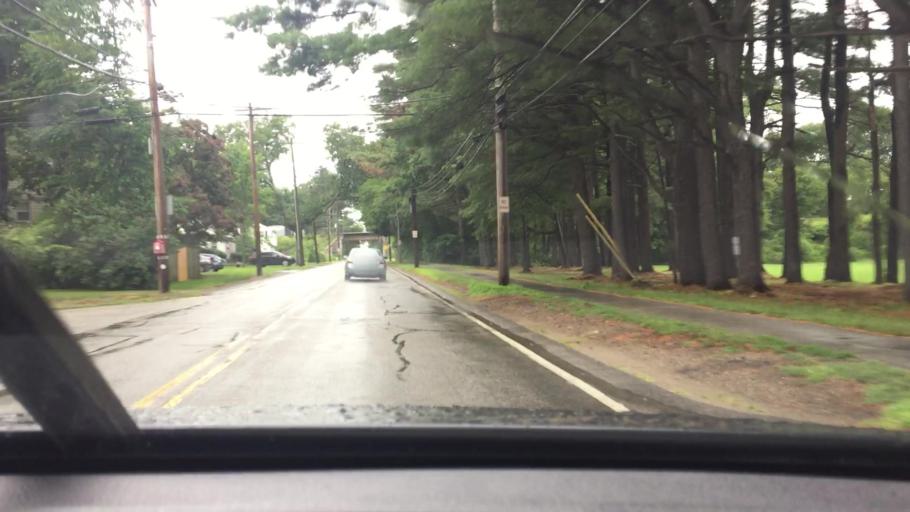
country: US
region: Massachusetts
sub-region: Norfolk County
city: Needham
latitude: 42.2729
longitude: -71.2257
